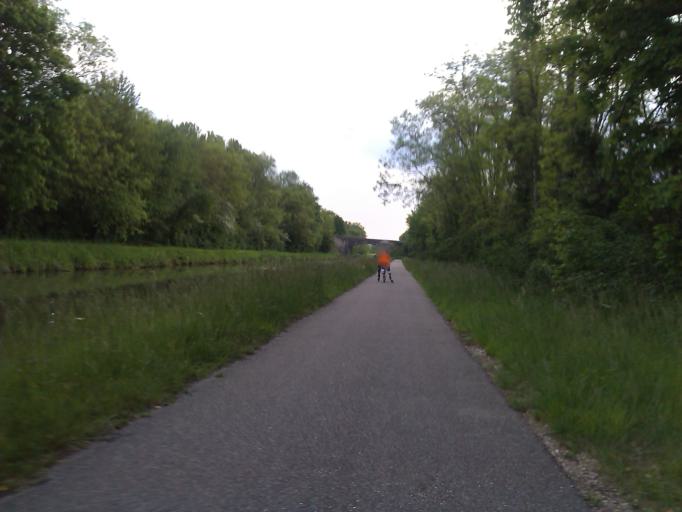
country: FR
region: Franche-Comte
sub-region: Departement du Jura
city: Dole
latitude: 47.0972
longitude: 5.5352
